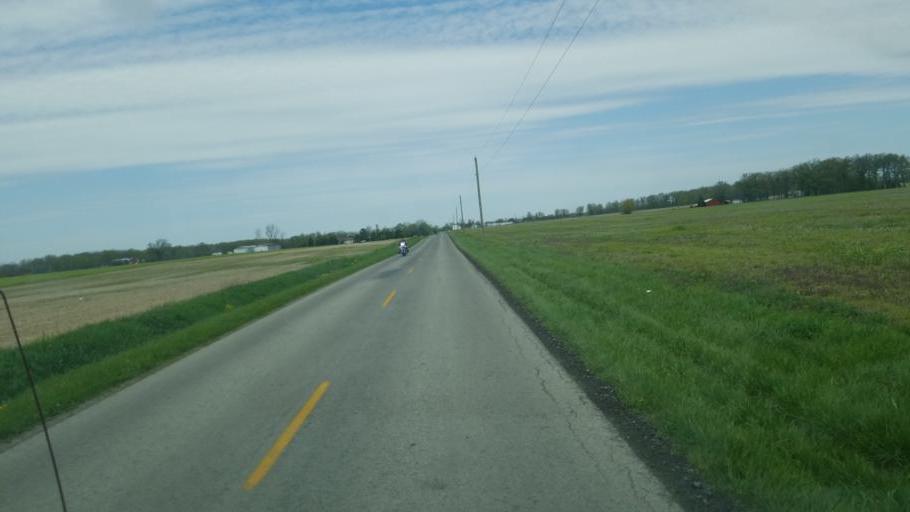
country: US
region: Ohio
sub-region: Allen County
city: Bluffton
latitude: 40.7921
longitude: -83.9724
